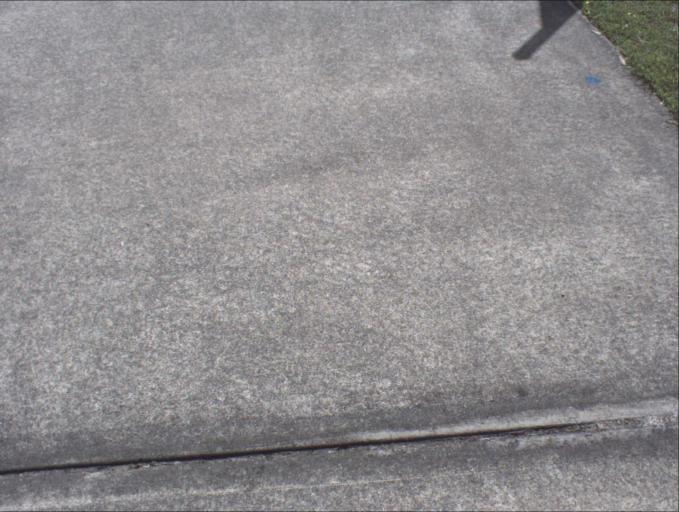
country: AU
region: Queensland
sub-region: Logan
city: Cedar Vale
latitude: -27.8298
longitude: 153.0263
